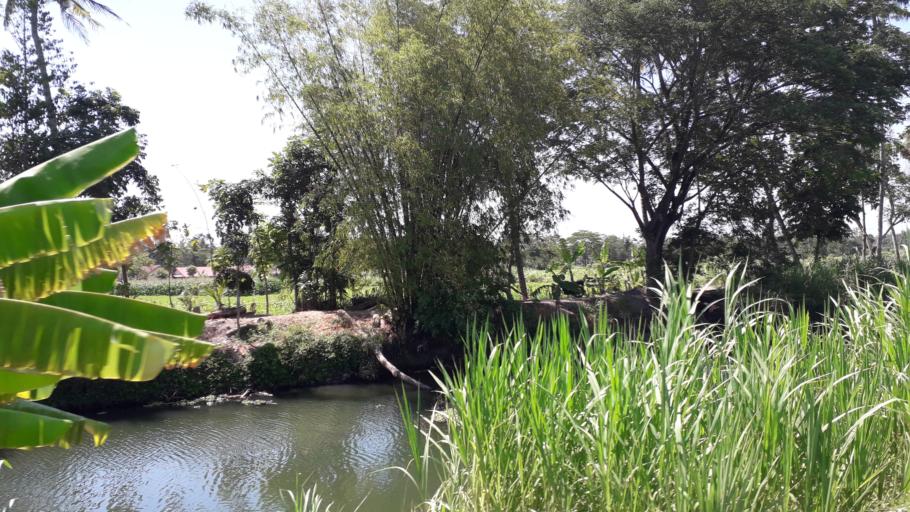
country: ID
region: Daerah Istimewa Yogyakarta
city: Pundong
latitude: -7.9506
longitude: 110.3273
